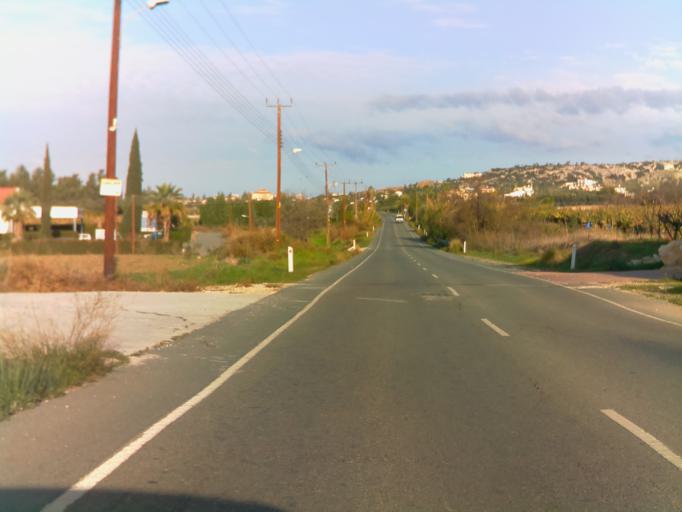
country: CY
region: Pafos
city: Pegeia
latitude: 34.8658
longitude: 32.3679
